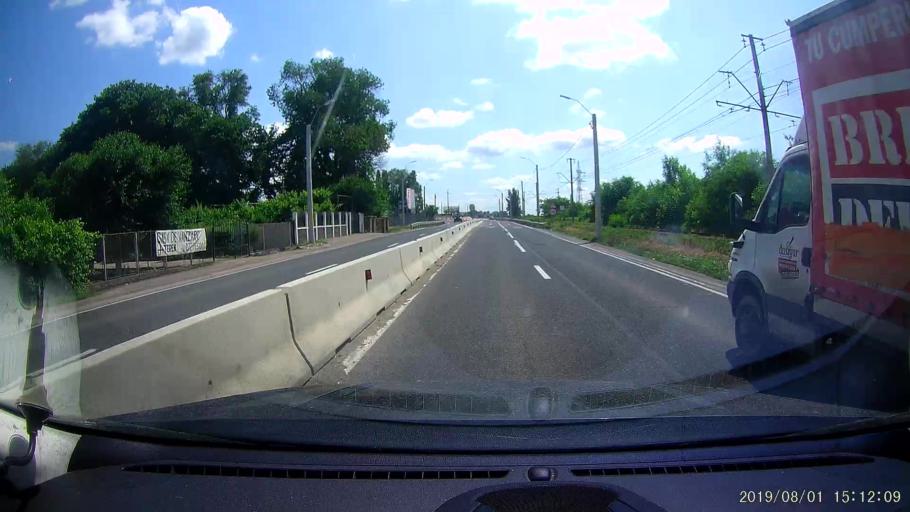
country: RO
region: Braila
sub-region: Comuna Chiscani
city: Lacu Sarat
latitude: 45.2088
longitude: 27.9162
